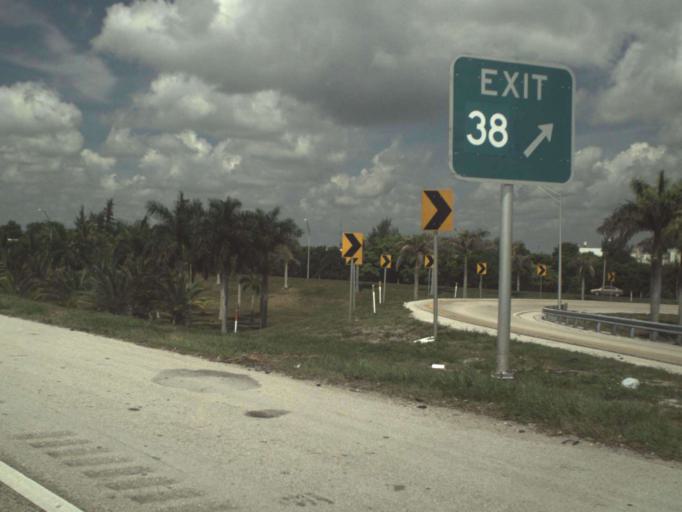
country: US
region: Florida
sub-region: Broward County
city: Kendall Green
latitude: 26.2588
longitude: -80.1349
